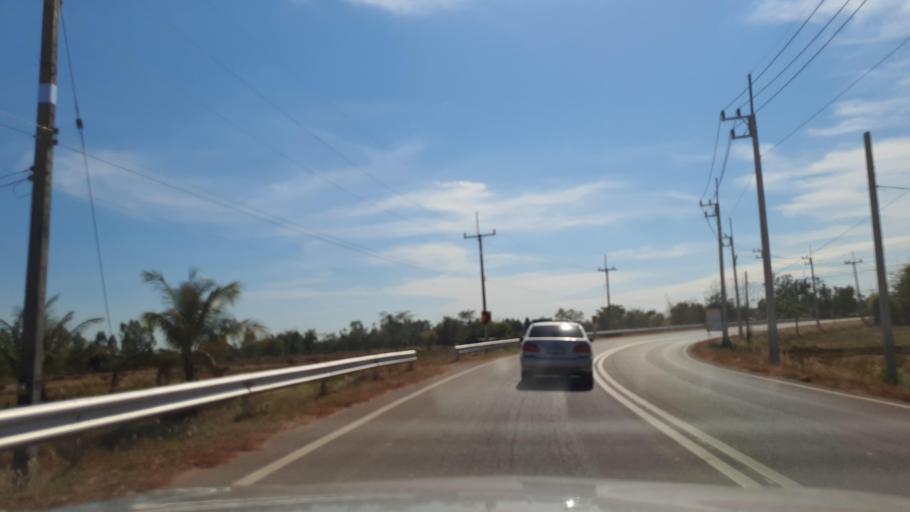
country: TH
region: Kalasin
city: Khao Wong
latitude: 16.7425
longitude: 104.1090
